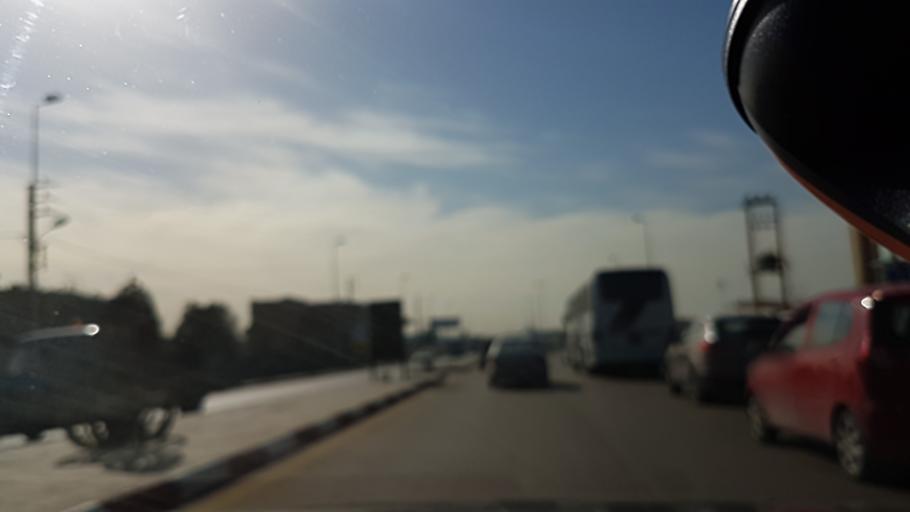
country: LB
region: Liban-Sud
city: Sidon
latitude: 33.5908
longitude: 35.3875
